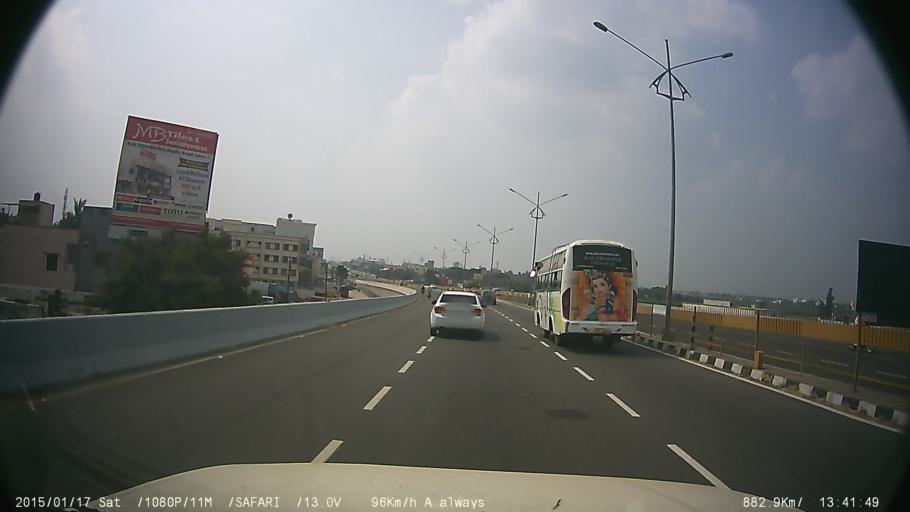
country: IN
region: Tamil Nadu
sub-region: Vellore
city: Vellore
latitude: 12.9349
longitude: 79.1487
